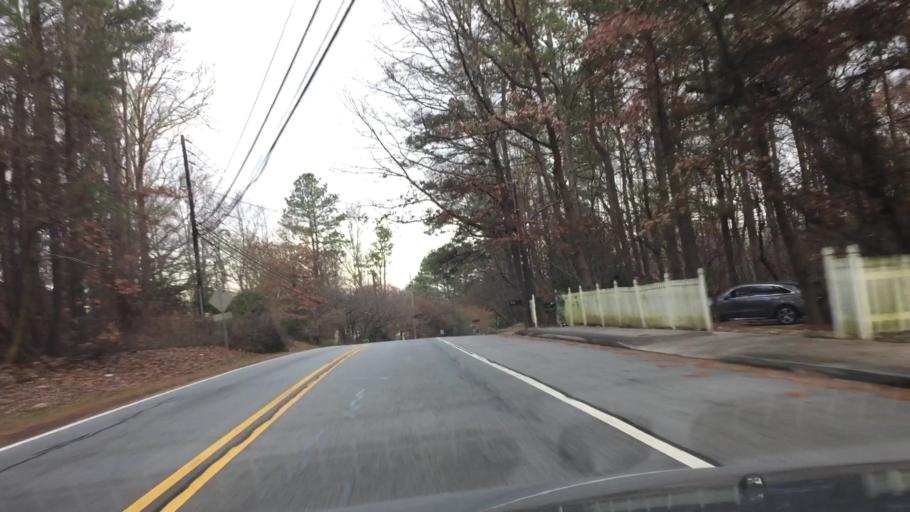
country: US
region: Georgia
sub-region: DeKalb County
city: Doraville
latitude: 33.9480
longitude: -84.2707
